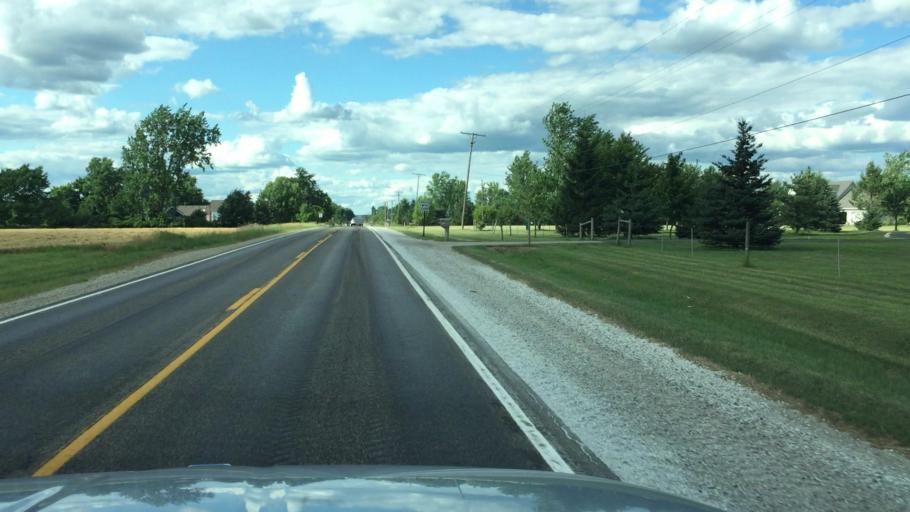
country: US
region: Michigan
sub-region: Saint Clair County
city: Capac
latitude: 43.0580
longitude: -82.9297
